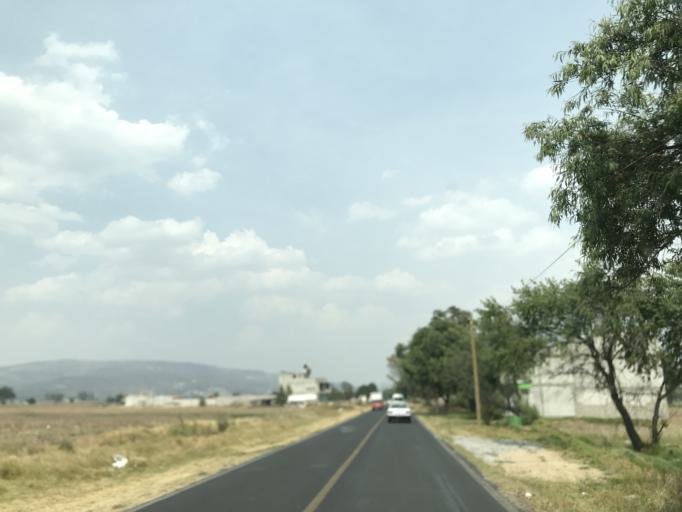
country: MX
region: Tlaxcala
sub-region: Ixtacuixtla de Mariano Matamoros
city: Santa Justina Ecatepec
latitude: 19.3146
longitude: -98.3300
